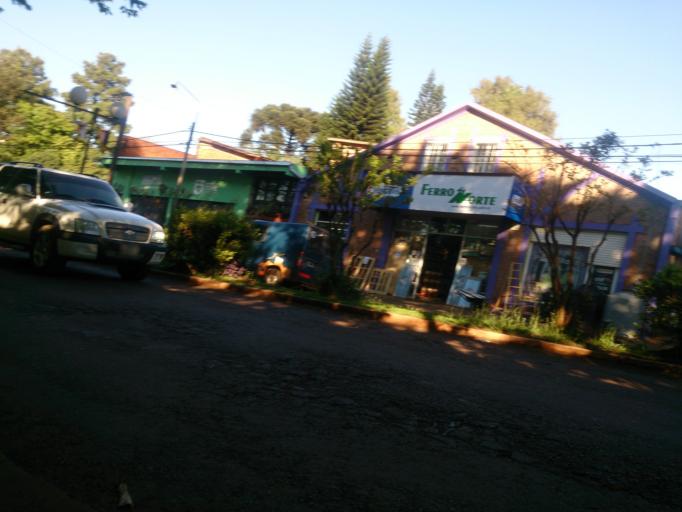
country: AR
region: Misiones
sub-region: Departamento de Obera
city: Obera
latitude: -27.4901
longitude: -55.1101
